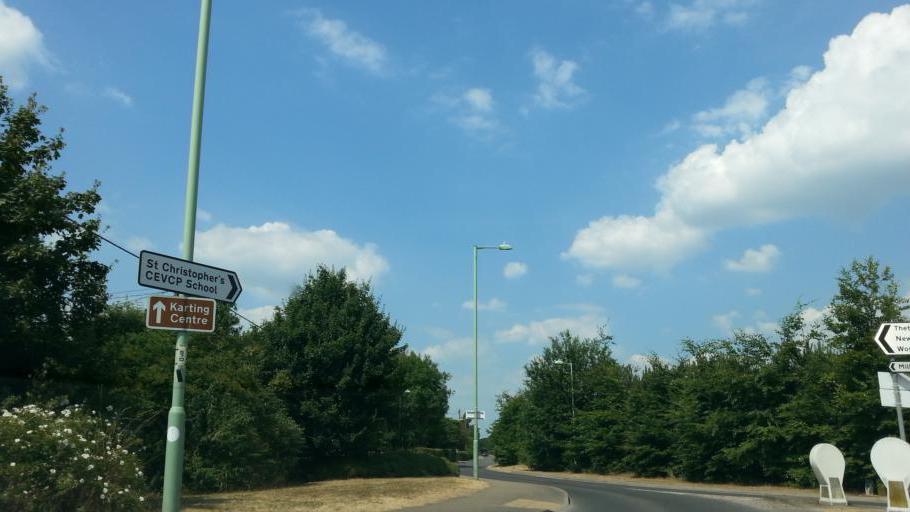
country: GB
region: England
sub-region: Cambridgeshire
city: Isleham
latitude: 52.3006
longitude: 0.4945
